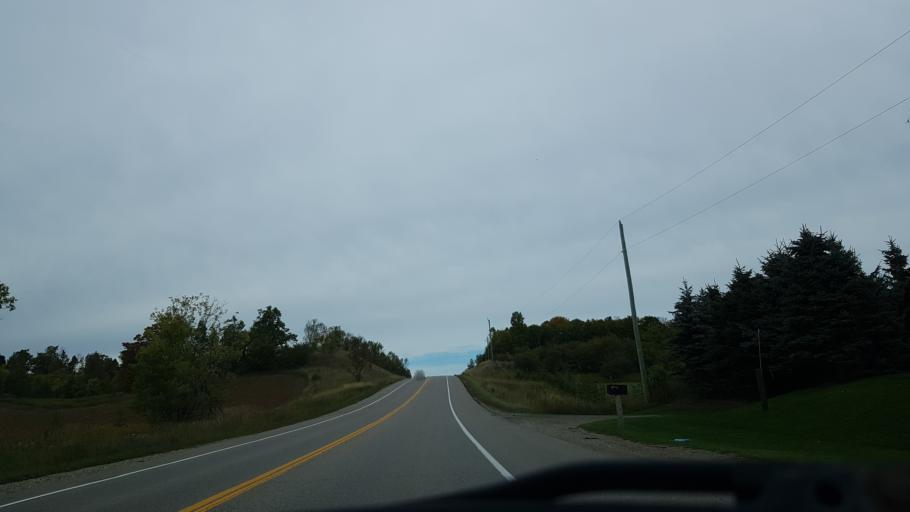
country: CA
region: Ontario
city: Orangeville
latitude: 44.0549
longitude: -80.0125
